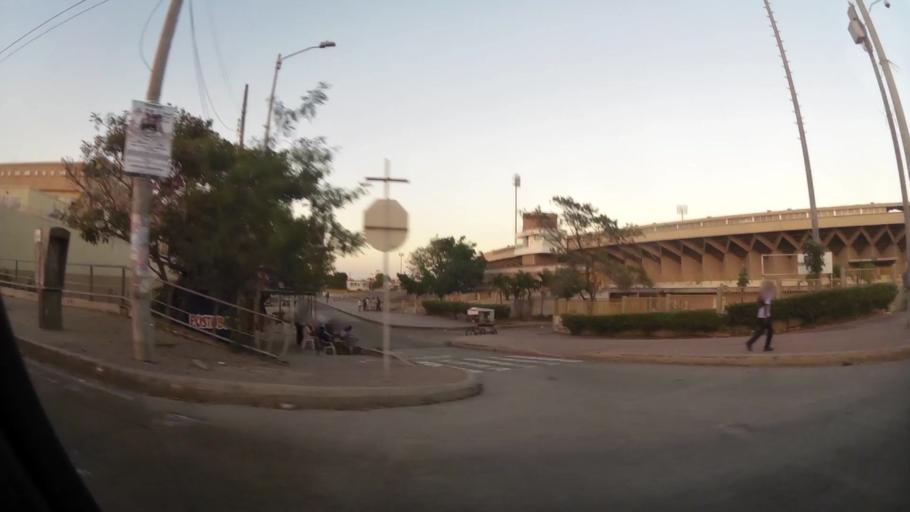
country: CO
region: Bolivar
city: Cartagena
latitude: 10.4053
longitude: -75.4996
